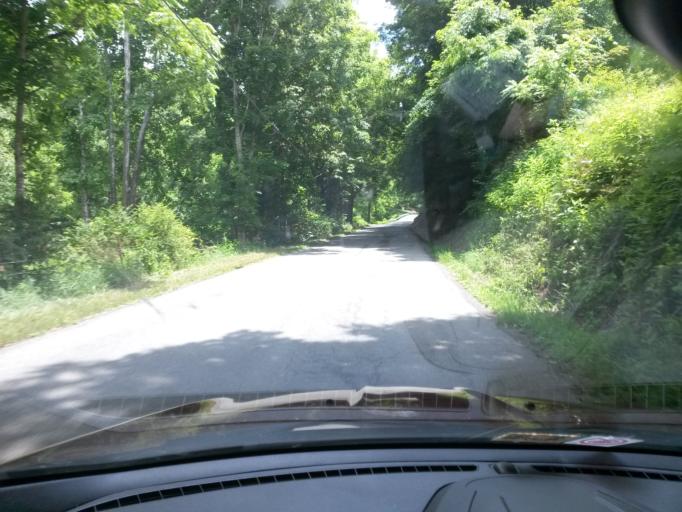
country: US
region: West Virginia
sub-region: Monroe County
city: Union
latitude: 37.5374
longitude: -80.5401
